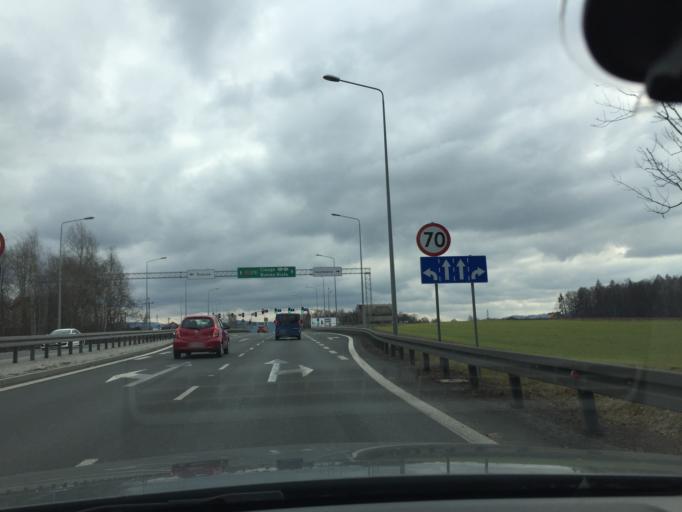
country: PL
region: Silesian Voivodeship
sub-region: Powiat bielski
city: Mazancowice
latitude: 49.8729
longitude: 19.0033
